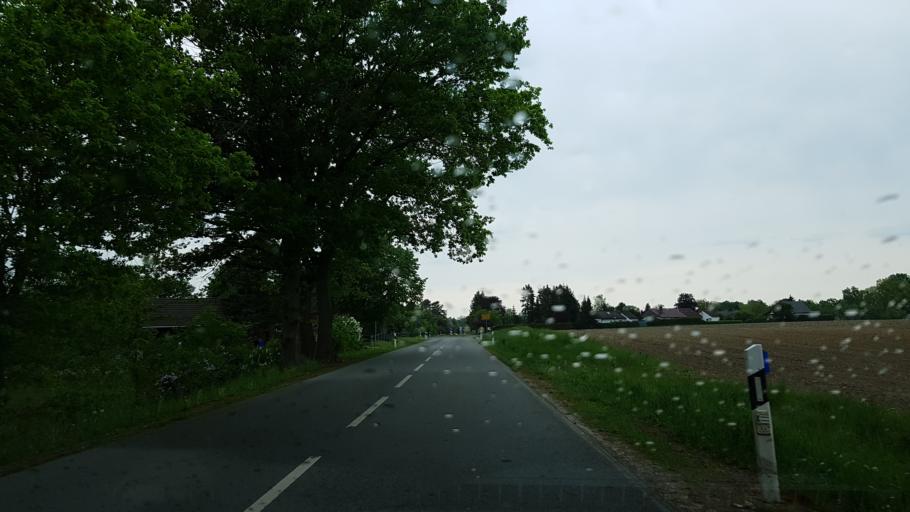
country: DE
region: Lower Saxony
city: Gorleben
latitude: 53.0655
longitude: 11.4113
